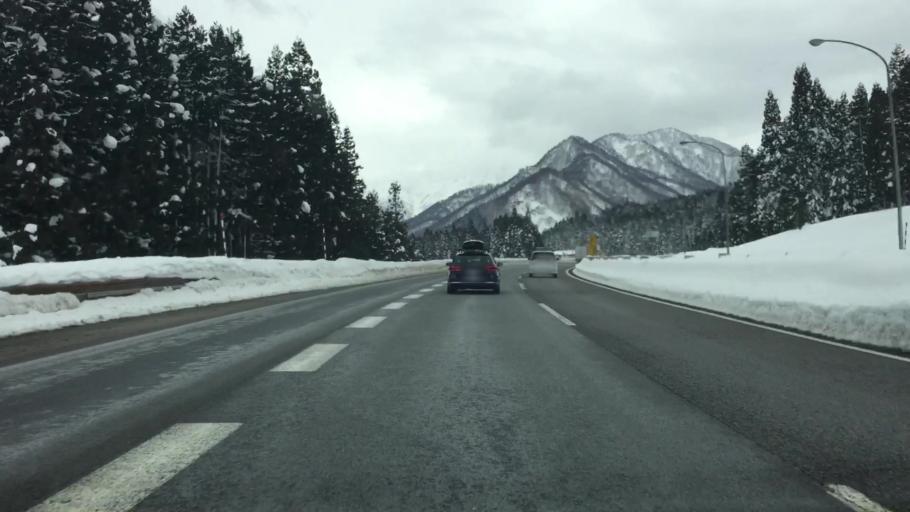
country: JP
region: Niigata
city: Shiozawa
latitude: 36.8912
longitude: 138.8475
